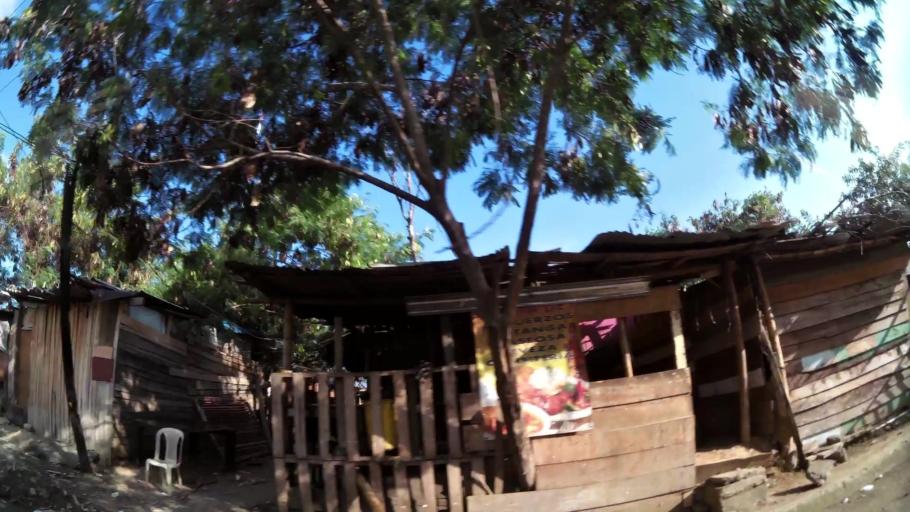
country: CO
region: Valle del Cauca
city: Cali
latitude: 3.4138
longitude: -76.4838
